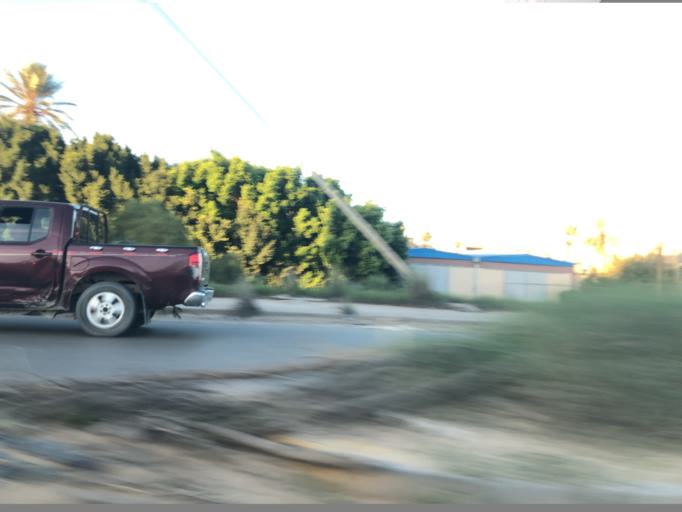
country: LY
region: Tripoli
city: Tagiura
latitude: 32.8694
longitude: 13.2864
